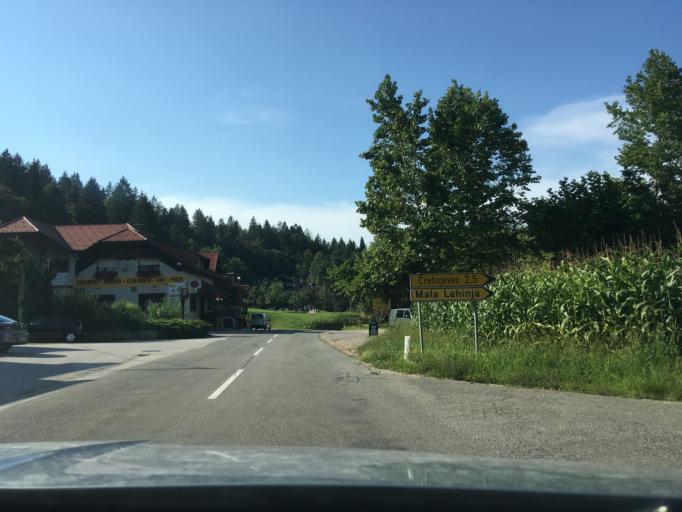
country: SI
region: Crnomelj
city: Crnomelj
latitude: 45.5015
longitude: 15.1905
